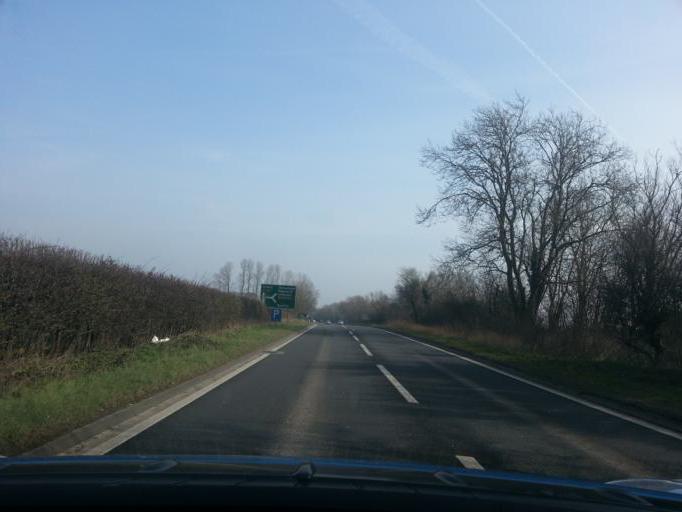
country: GB
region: England
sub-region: Oxfordshire
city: Shrivenham
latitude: 51.5882
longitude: -1.6785
